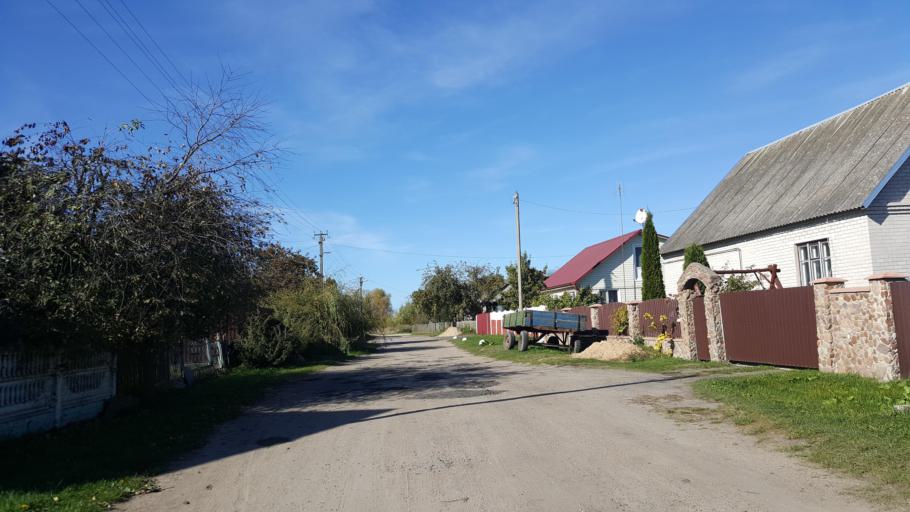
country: BY
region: Brest
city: Kamyanyets
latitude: 52.4021
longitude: 23.7912
